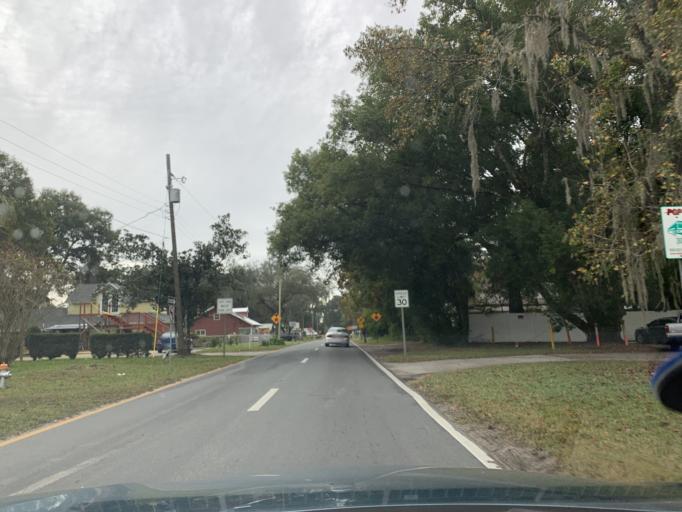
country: US
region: Florida
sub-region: Pasco County
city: Zephyrhills
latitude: 28.2300
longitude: -82.1811
